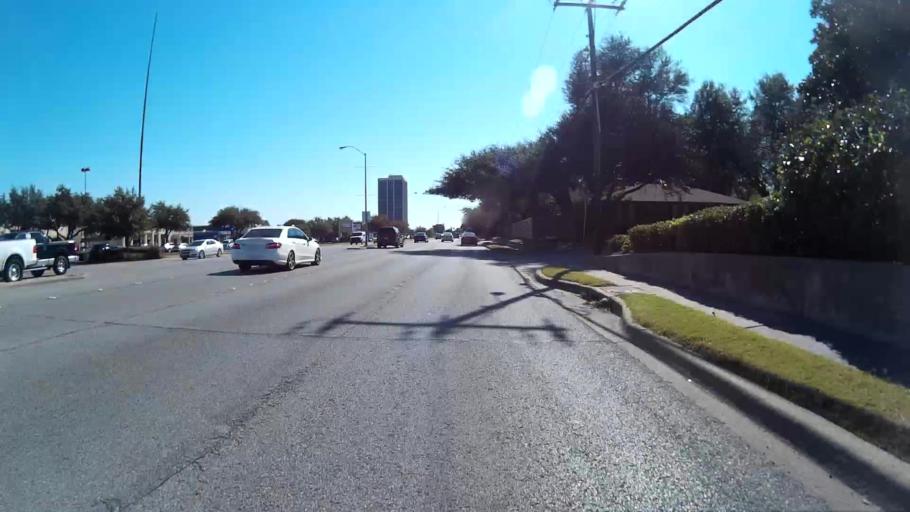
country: US
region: Texas
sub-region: Dallas County
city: Richardson
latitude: 32.9598
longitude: -96.7690
